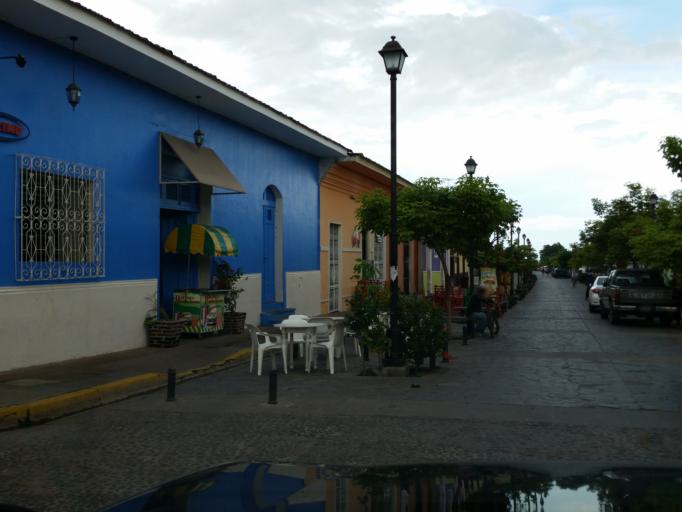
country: NI
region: Granada
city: Granada
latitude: 11.9301
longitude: -85.9504
